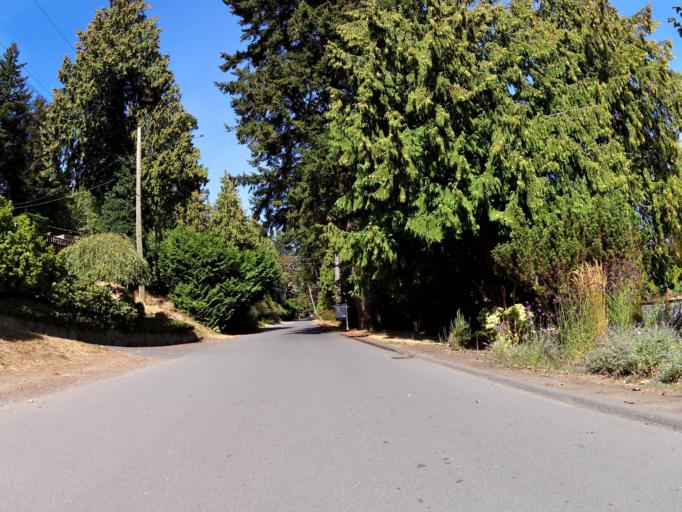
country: CA
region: British Columbia
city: Victoria
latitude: 48.5151
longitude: -123.3676
